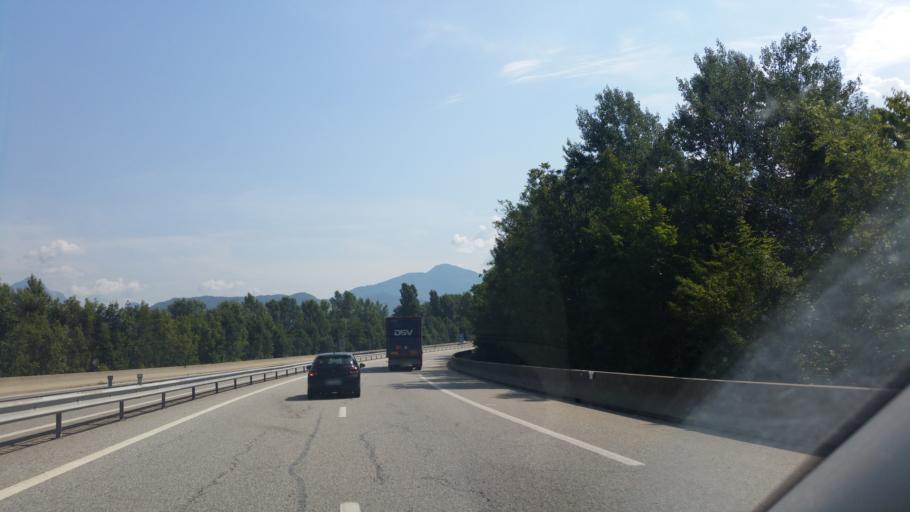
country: FR
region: Rhone-Alpes
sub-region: Departement de la Savoie
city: Gilly-sur-Isere
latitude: 45.6480
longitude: 6.3357
